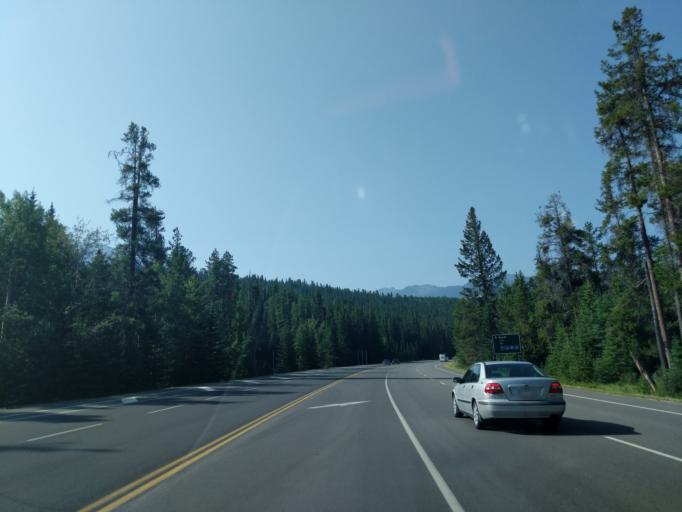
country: CA
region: Alberta
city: Banff
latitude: 51.1992
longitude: -115.5377
